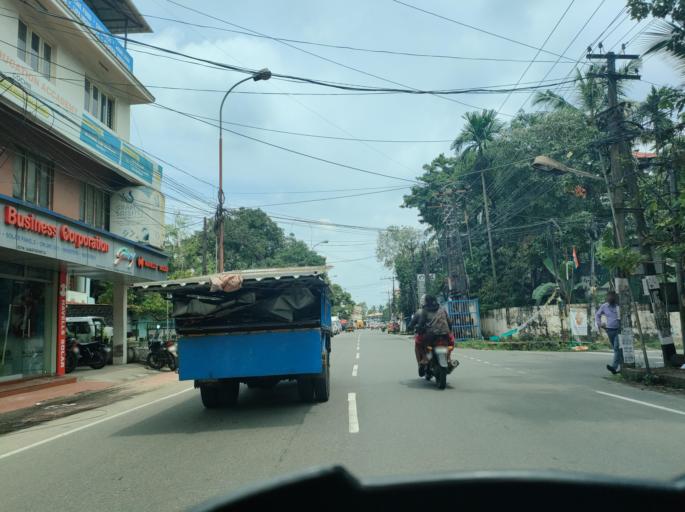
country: IN
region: Kerala
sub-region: Ernakulam
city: Cochin
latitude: 9.9742
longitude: 76.3127
